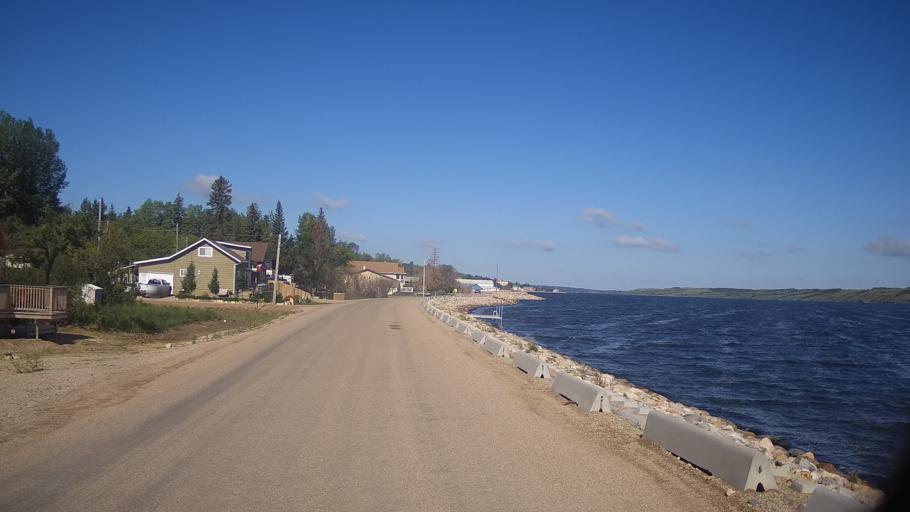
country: CA
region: Saskatchewan
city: Watrous
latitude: 51.7185
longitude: -105.4256
